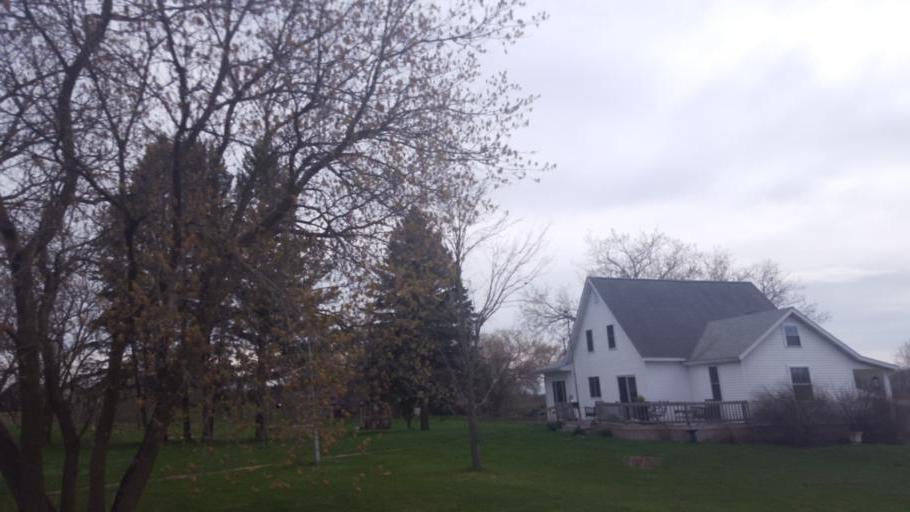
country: US
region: Michigan
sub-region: Clare County
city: Clare
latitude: 43.8731
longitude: -84.7154
